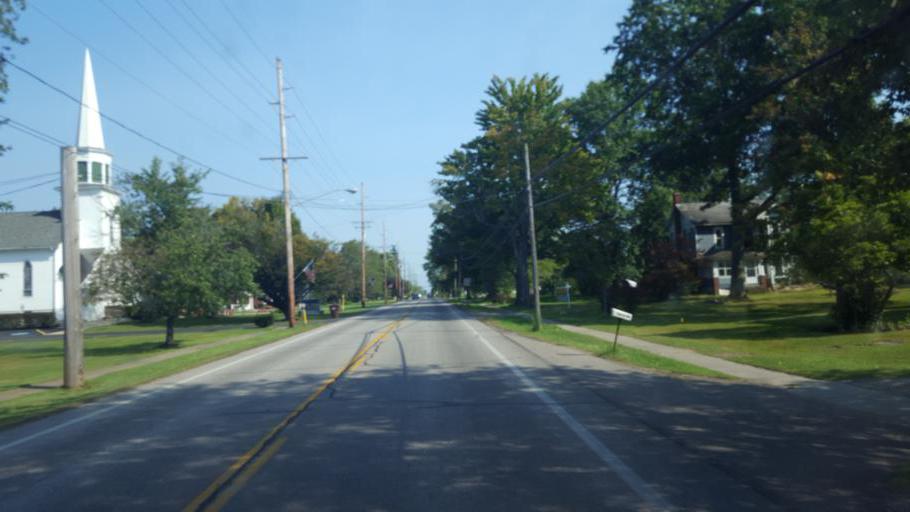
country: US
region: Ohio
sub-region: Ashtabula County
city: Orwell
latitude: 41.5382
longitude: -80.8676
